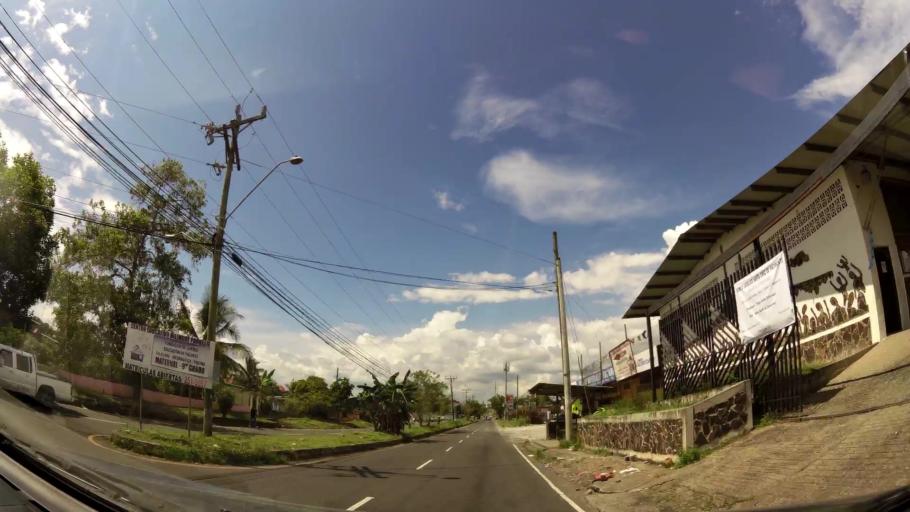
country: PA
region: Panama
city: Nuevo Arraijan
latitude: 8.9149
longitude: -79.7009
